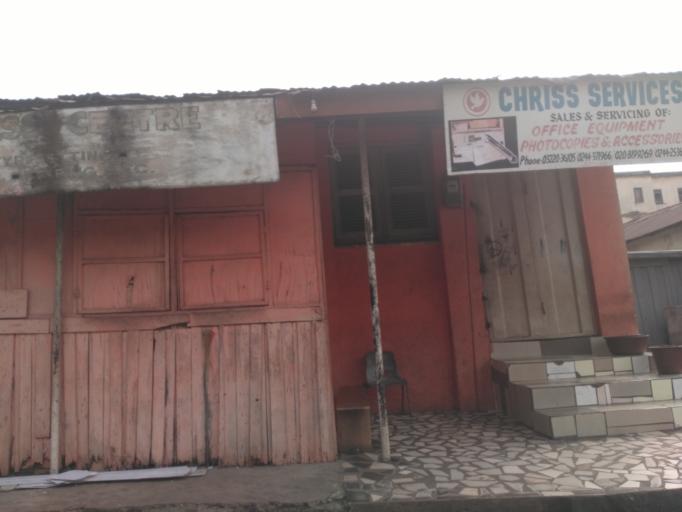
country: GH
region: Ashanti
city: Kumasi
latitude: 6.6906
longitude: -1.6166
